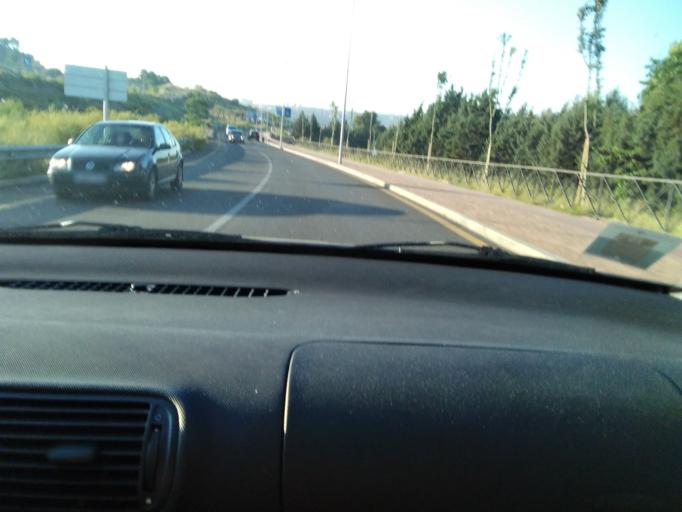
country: ES
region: Castille-La Mancha
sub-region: Province of Toledo
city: Toledo
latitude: 39.8847
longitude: -4.0548
